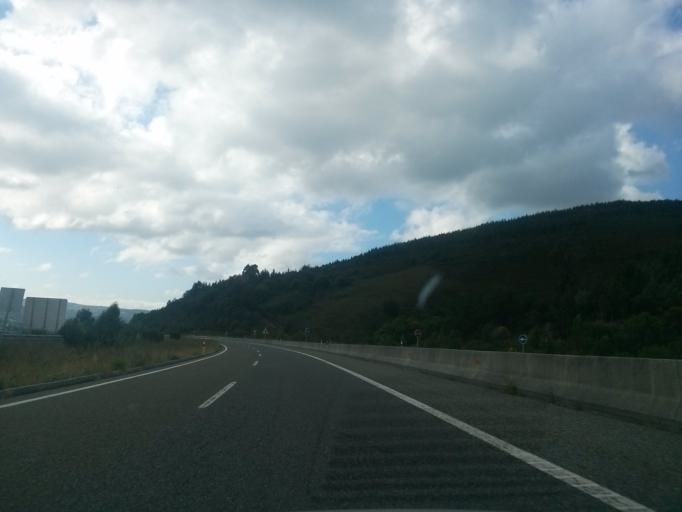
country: ES
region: Galicia
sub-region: Provincia de Lugo
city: Becerrea
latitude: 42.8849
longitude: -7.1773
